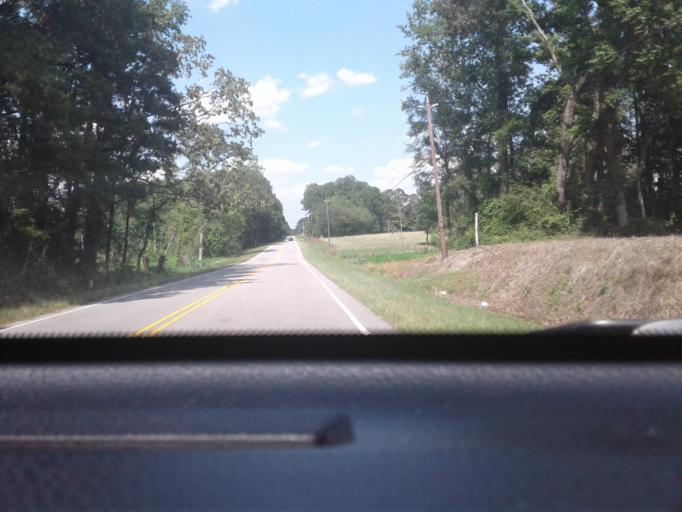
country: US
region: North Carolina
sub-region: Cumberland County
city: Eastover
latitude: 35.1769
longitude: -78.7159
